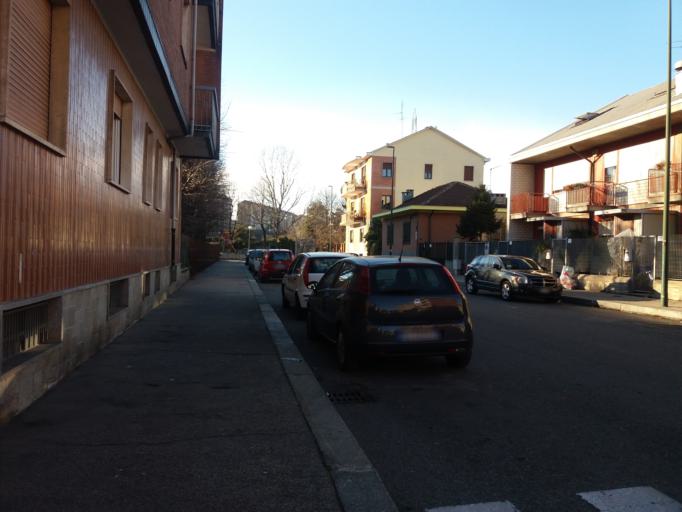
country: IT
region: Piedmont
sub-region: Provincia di Torino
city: Fornaci
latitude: 45.0191
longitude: 7.6217
